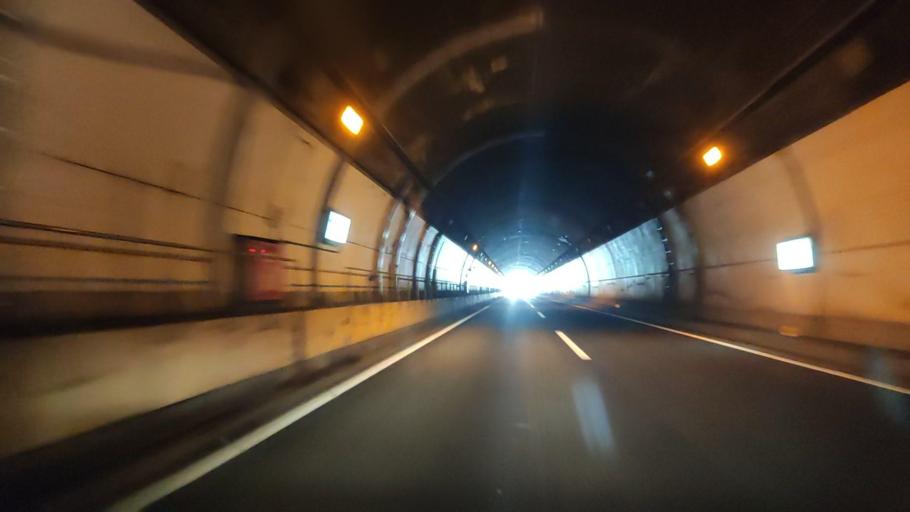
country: JP
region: Akita
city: Hanawa
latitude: 40.0175
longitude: 140.9853
